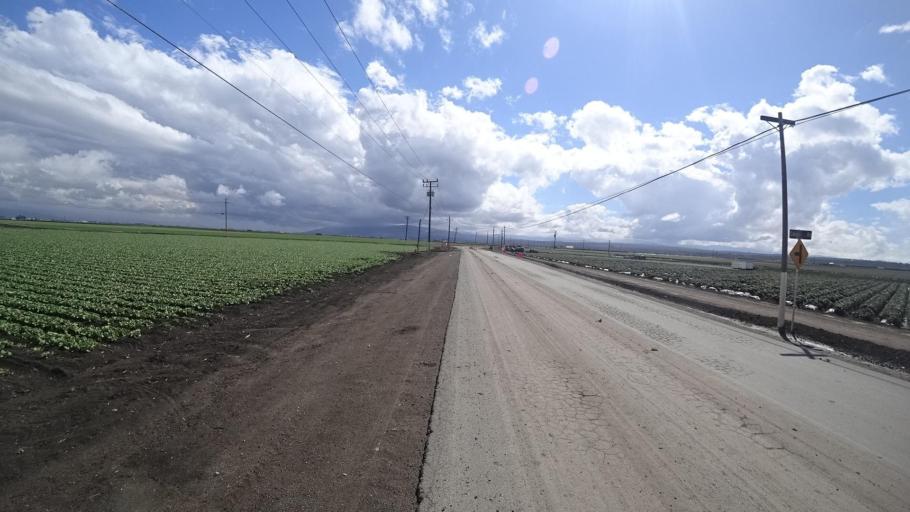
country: US
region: California
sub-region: Monterey County
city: Boronda
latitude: 36.7026
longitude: -121.7315
